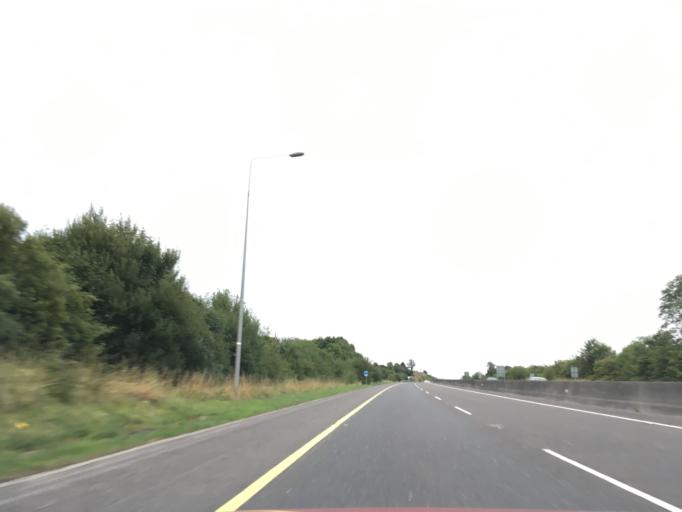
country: IE
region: Munster
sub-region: An Clar
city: Ennis
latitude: 52.8571
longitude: -8.9368
